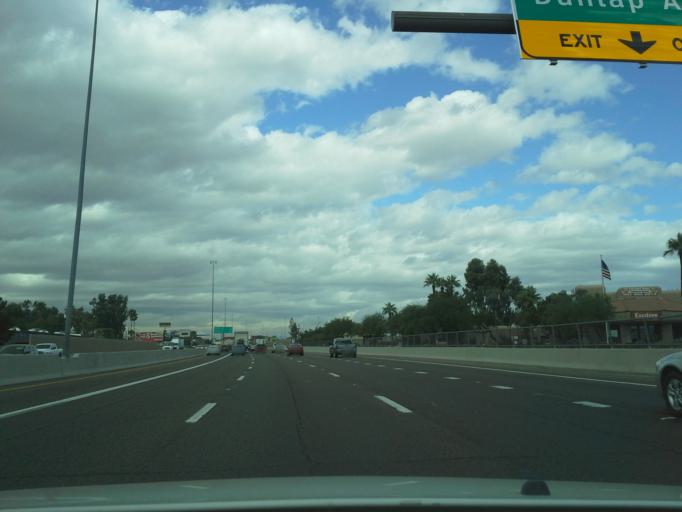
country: US
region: Arizona
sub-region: Maricopa County
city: Glendale
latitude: 33.5583
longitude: -112.1133
